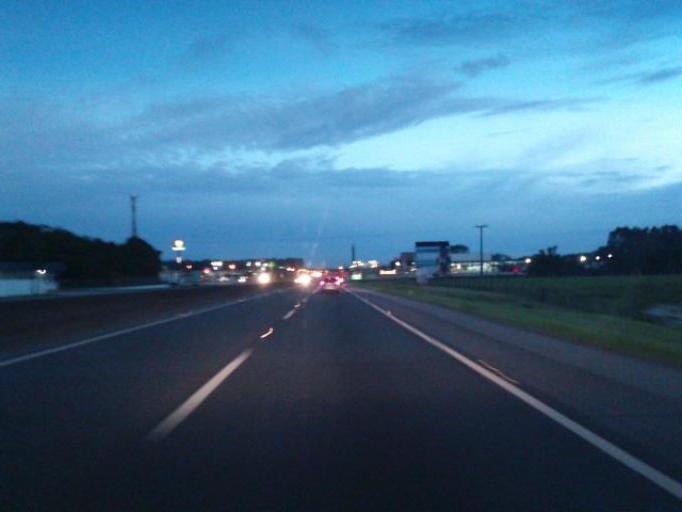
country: BR
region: Santa Catarina
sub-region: Barra Velha
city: Barra Velha
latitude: -26.5128
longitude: -48.7223
